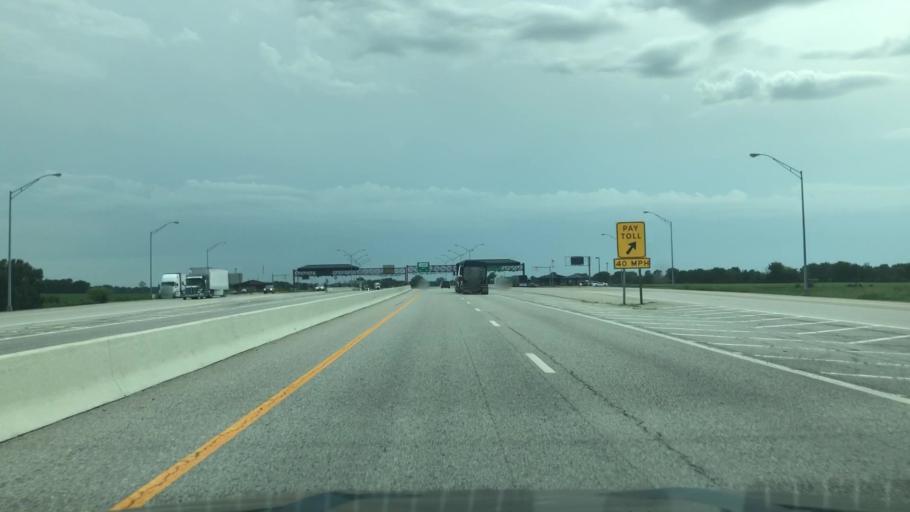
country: US
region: Oklahoma
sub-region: Craig County
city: Vinita
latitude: 36.6068
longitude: -95.1846
